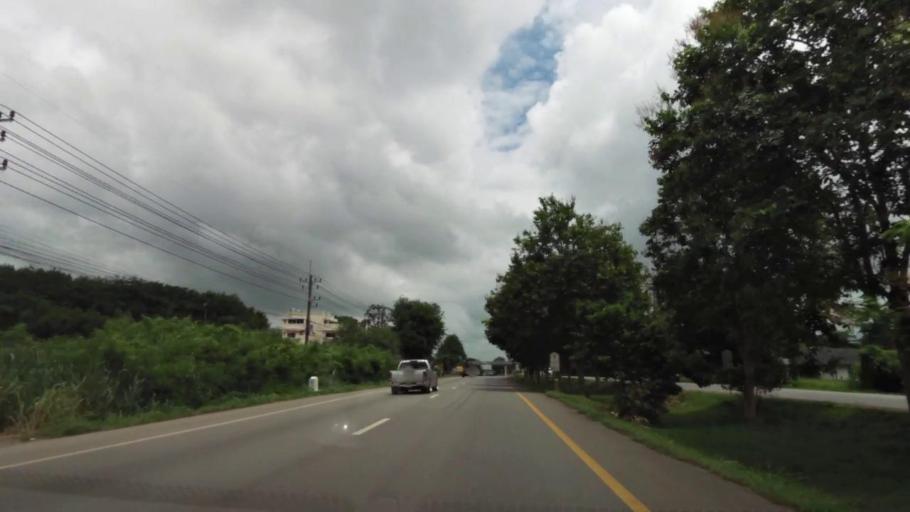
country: TH
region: Chanthaburi
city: Na Yai Am
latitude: 12.7693
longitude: 101.8465
